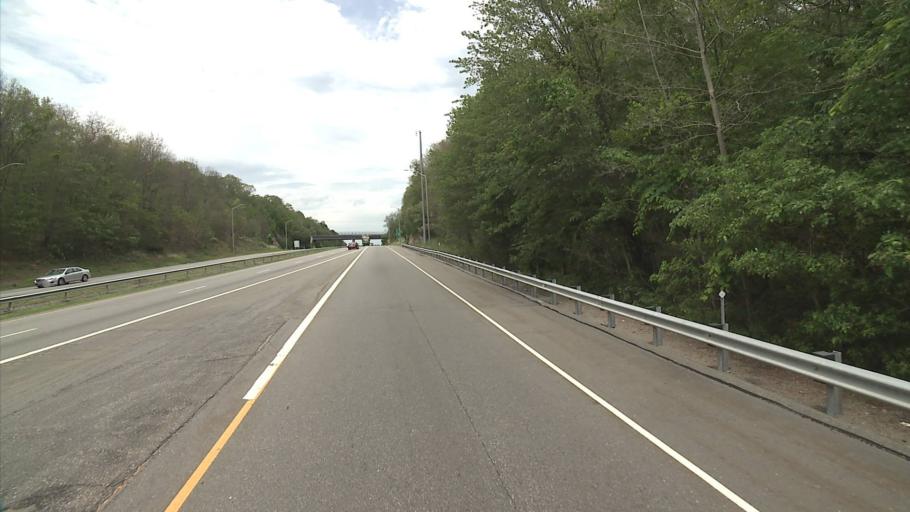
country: US
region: Connecticut
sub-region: New London County
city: Montville Center
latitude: 41.4906
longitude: -72.1141
